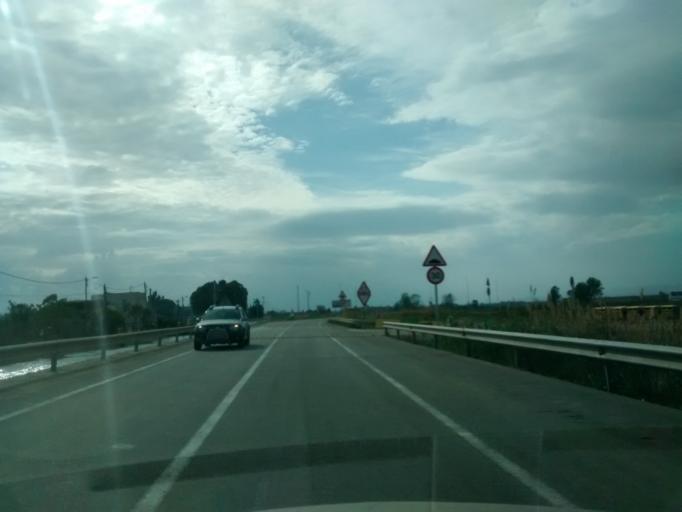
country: ES
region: Catalonia
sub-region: Provincia de Tarragona
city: Deltebre
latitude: 40.7047
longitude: 0.7134
